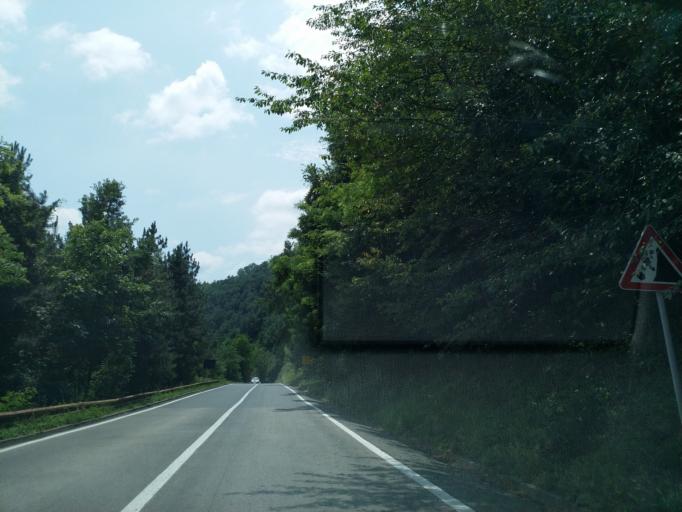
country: RS
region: Central Serbia
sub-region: Rasinski Okrug
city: Aleksandrovac
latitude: 43.4103
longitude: 21.1558
